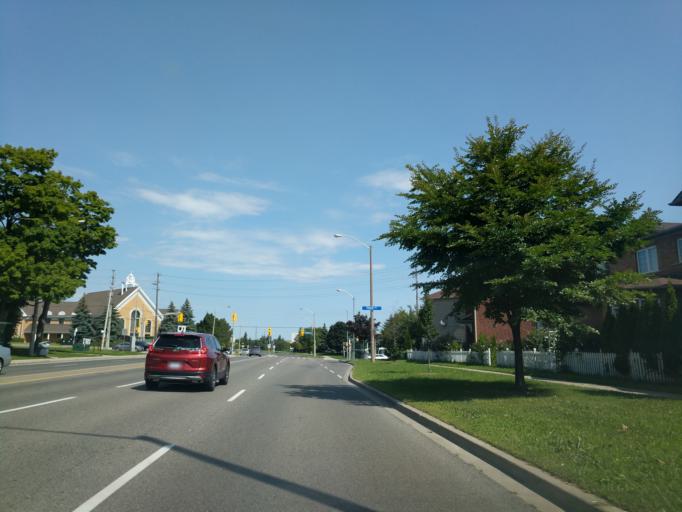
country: CA
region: Ontario
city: Scarborough
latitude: 43.8155
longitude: -79.2271
